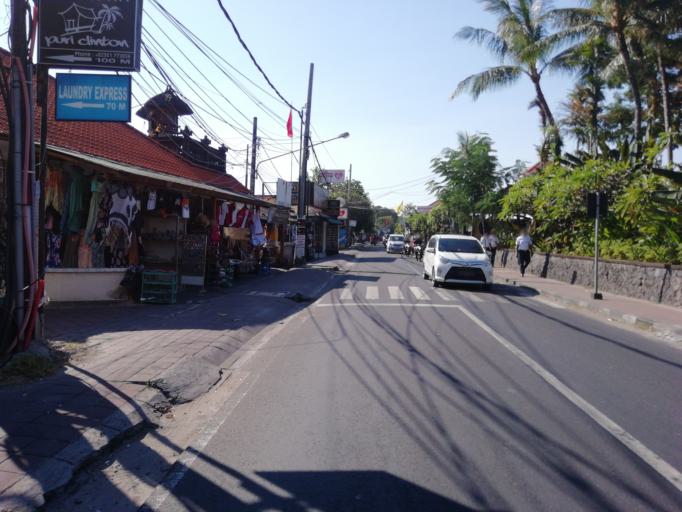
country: ID
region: Bali
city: Bualu
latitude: -8.7811
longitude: 115.2243
